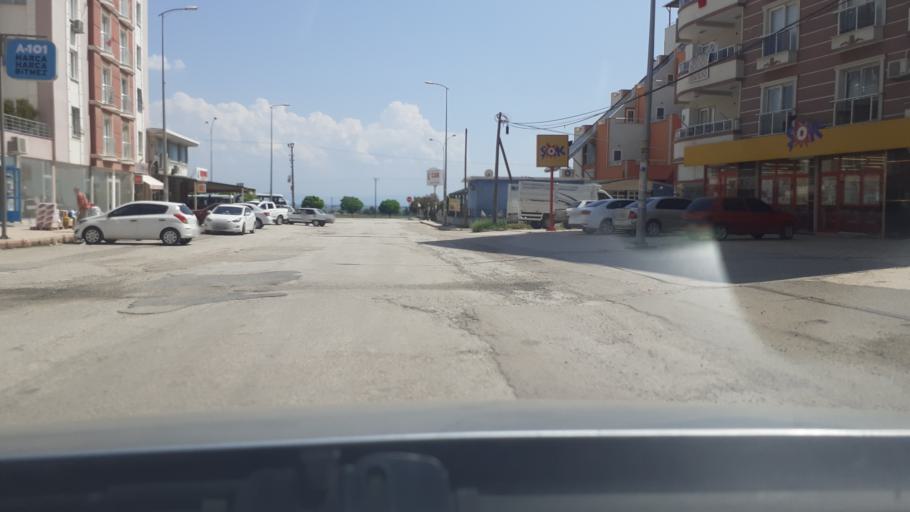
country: TR
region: Hatay
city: Kirikhan
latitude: 36.4807
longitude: 36.3557
